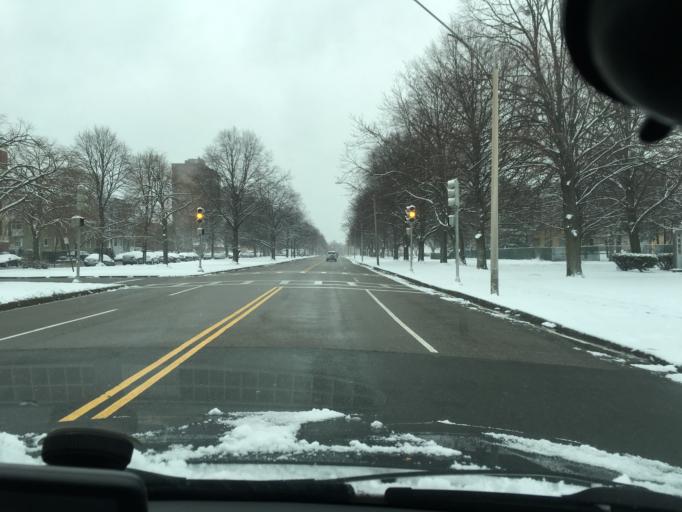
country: US
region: Massachusetts
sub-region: Suffolk County
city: South Boston
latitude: 42.3301
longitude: -71.0478
